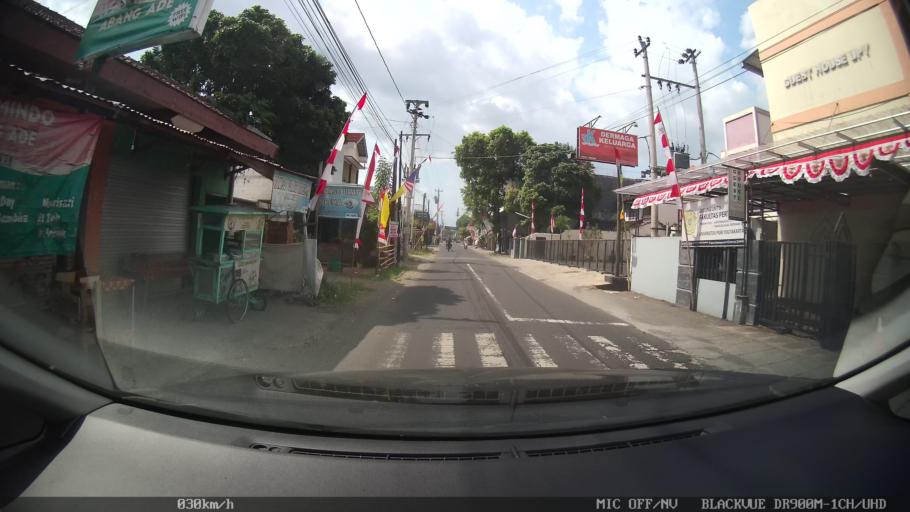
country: ID
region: Daerah Istimewa Yogyakarta
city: Gamping Lor
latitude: -7.8090
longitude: 110.3388
